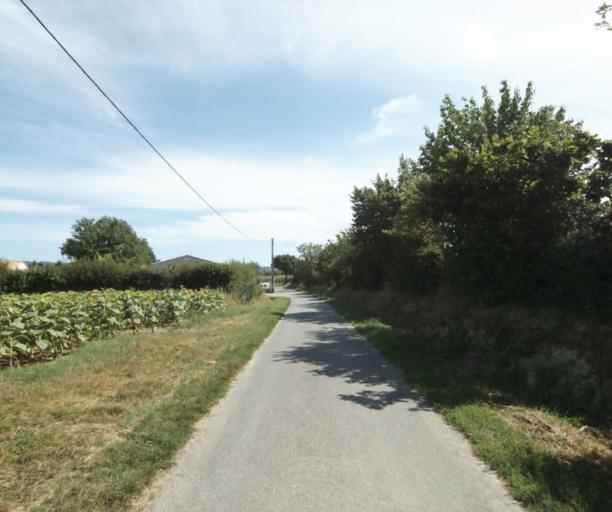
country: FR
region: Midi-Pyrenees
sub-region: Departement de la Haute-Garonne
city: Revel
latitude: 43.5090
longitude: 2.0299
